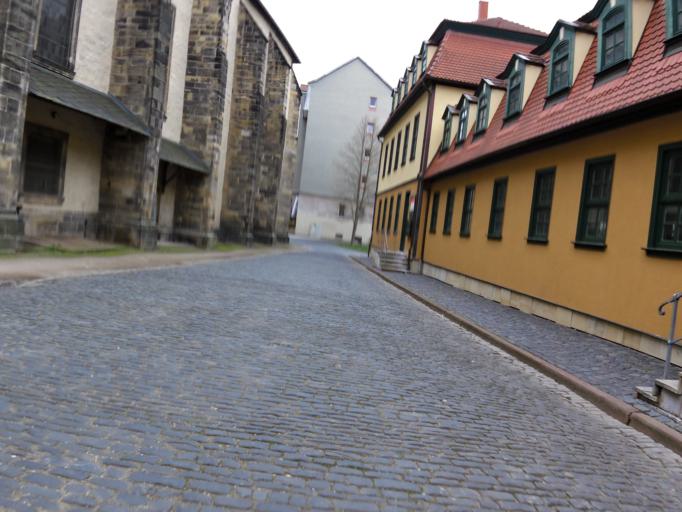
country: DE
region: Thuringia
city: Gotha
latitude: 50.9505
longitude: 10.7047
